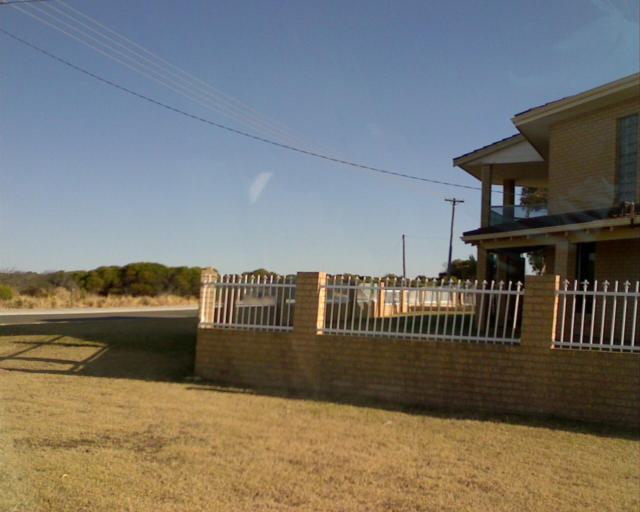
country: AU
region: Western Australia
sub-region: Dandaragan
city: Jurien Bay
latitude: -30.0651
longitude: 114.9662
